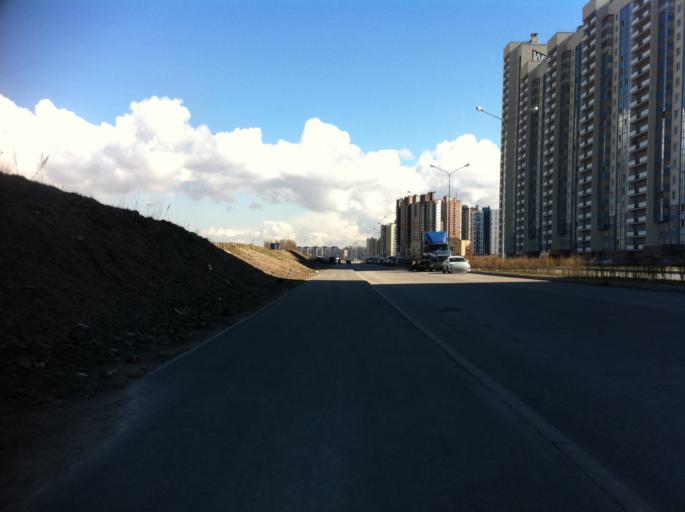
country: RU
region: St.-Petersburg
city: Uritsk
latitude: 59.8670
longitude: 30.1771
